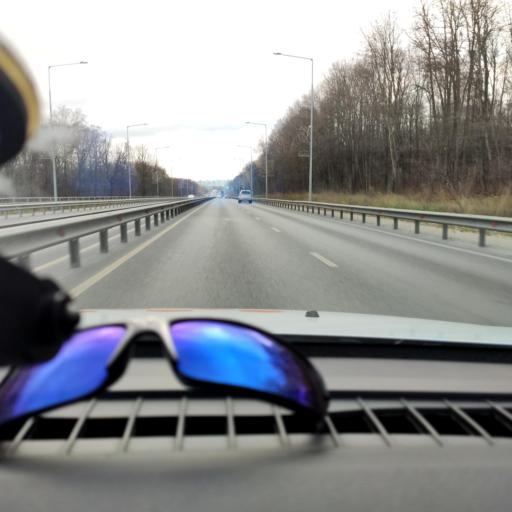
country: RU
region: Samara
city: Volzhskiy
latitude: 53.3609
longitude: 50.2042
